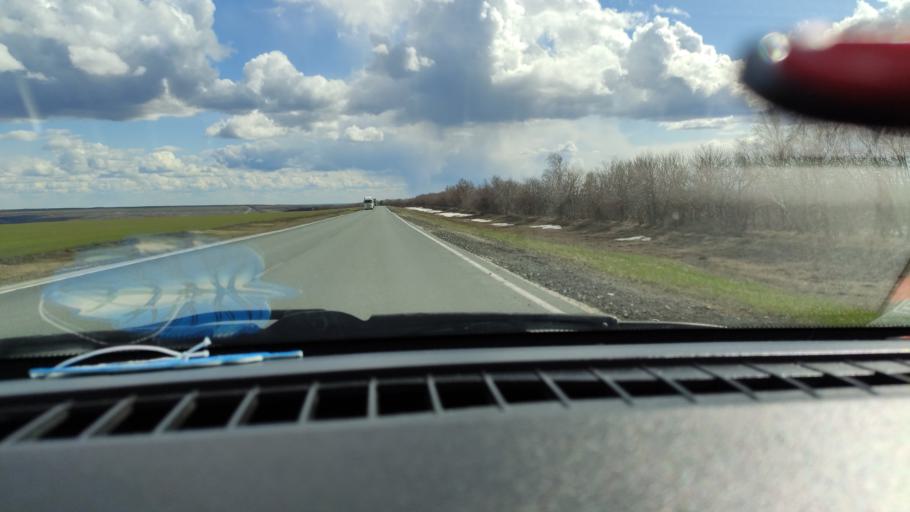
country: RU
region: Saratov
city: Dukhovnitskoye
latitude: 52.7680
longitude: 48.2376
